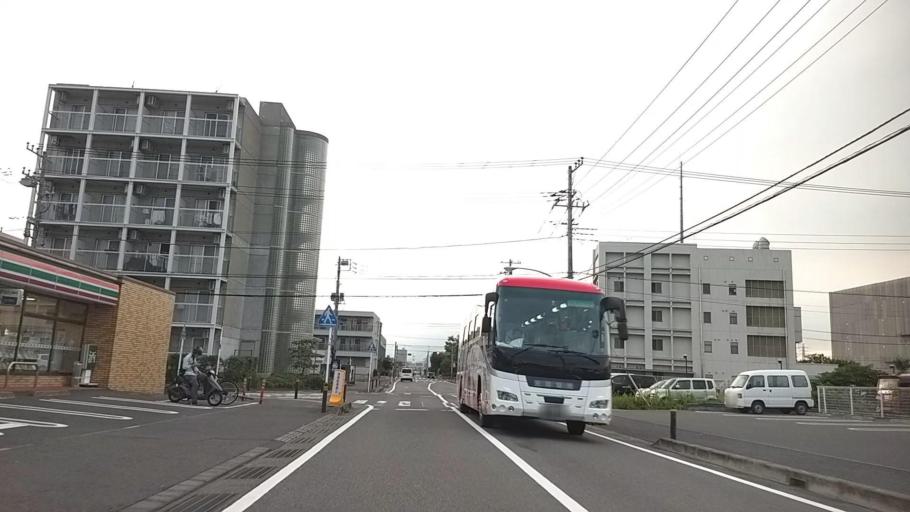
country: JP
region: Kanagawa
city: Atsugi
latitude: 35.4451
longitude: 139.3929
